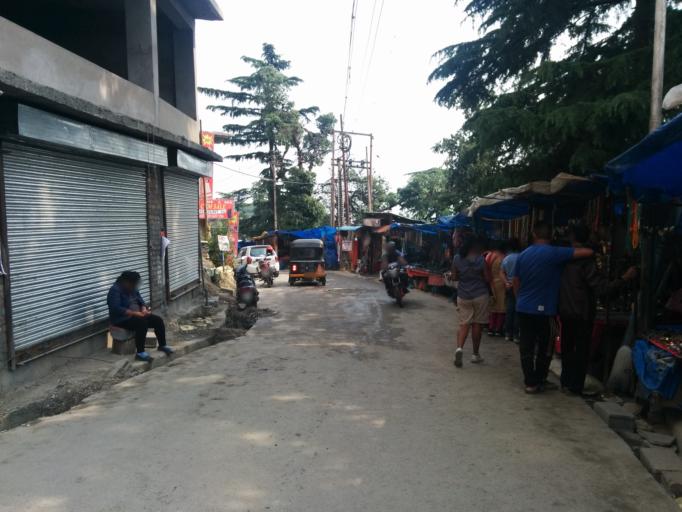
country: IN
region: Himachal Pradesh
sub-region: Kangra
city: Dharmsala
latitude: 32.2360
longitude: 76.3238
